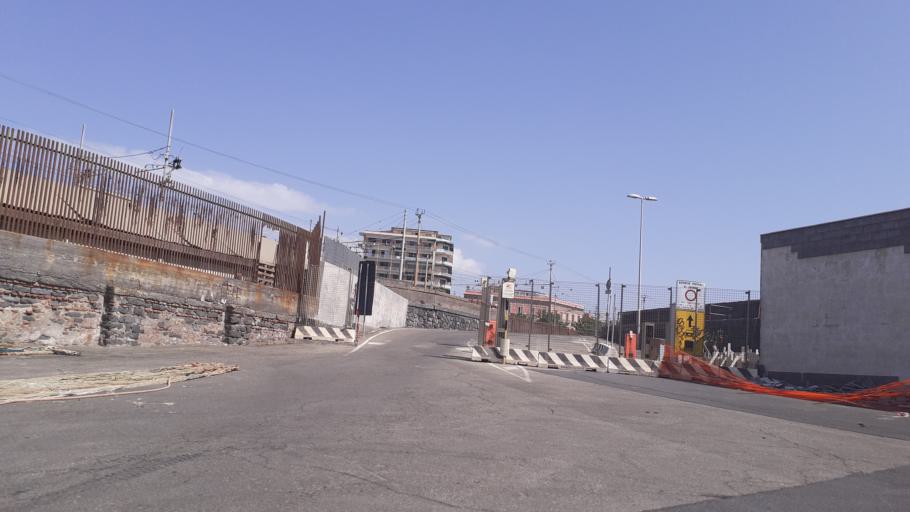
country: IT
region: Sicily
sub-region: Catania
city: Catania
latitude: 37.5025
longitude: 15.0964
